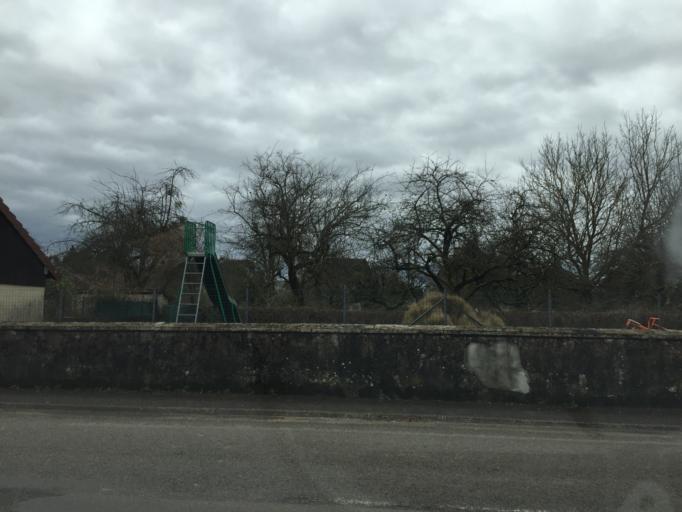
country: FR
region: Franche-Comte
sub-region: Departement du Doubs
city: Arc-et-Senans
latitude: 47.0217
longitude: 5.7211
